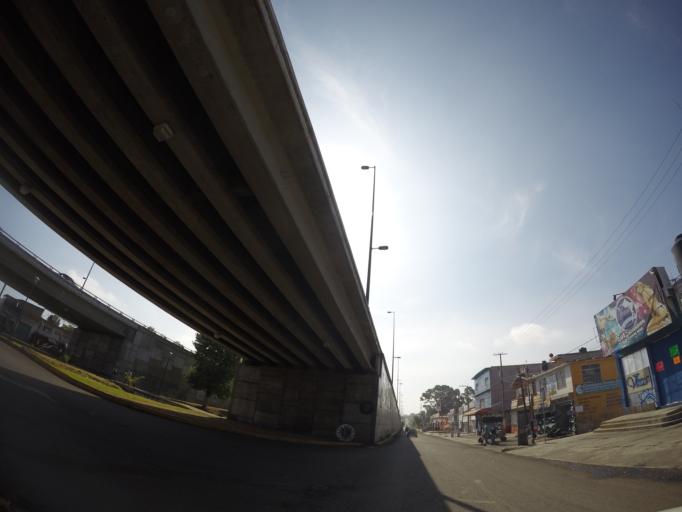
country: MX
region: Michoacan
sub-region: Tarimbaro
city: Real Hacienda (Metropolis)
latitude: 19.7254
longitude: -101.2048
